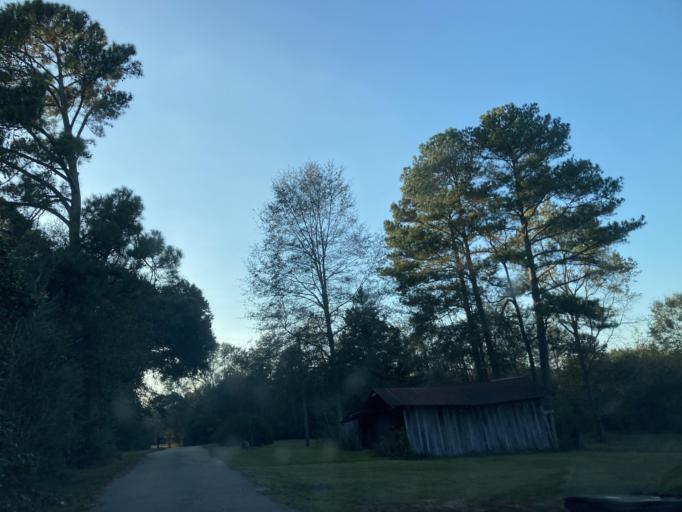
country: US
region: Mississippi
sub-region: Lamar County
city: Sumrall
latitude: 31.3940
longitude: -89.5927
